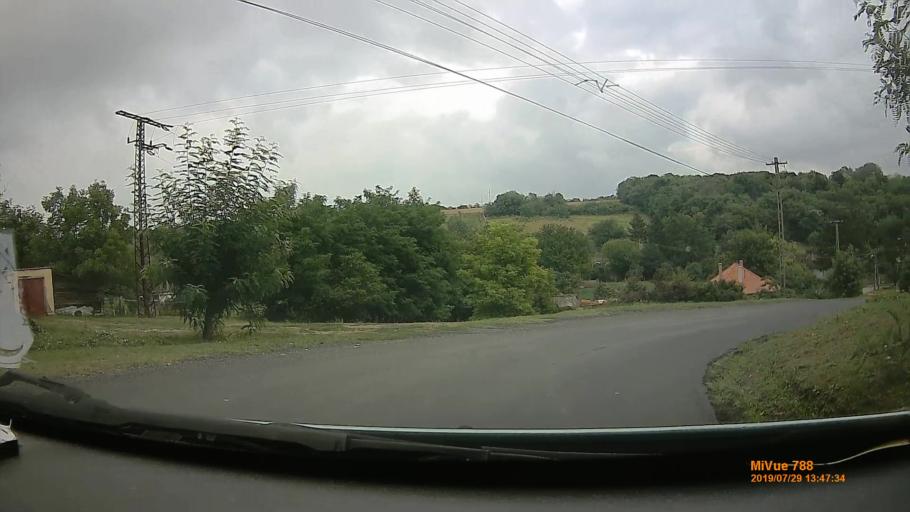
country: HU
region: Somogy
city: Balatonfoldvar
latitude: 46.7850
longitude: 17.9490
